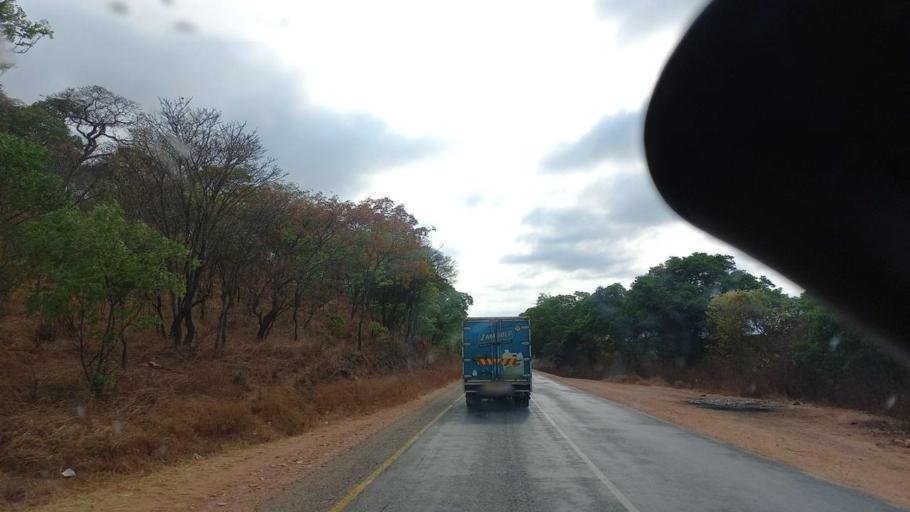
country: ZM
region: Lusaka
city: Chongwe
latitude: -15.2708
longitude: 28.8963
